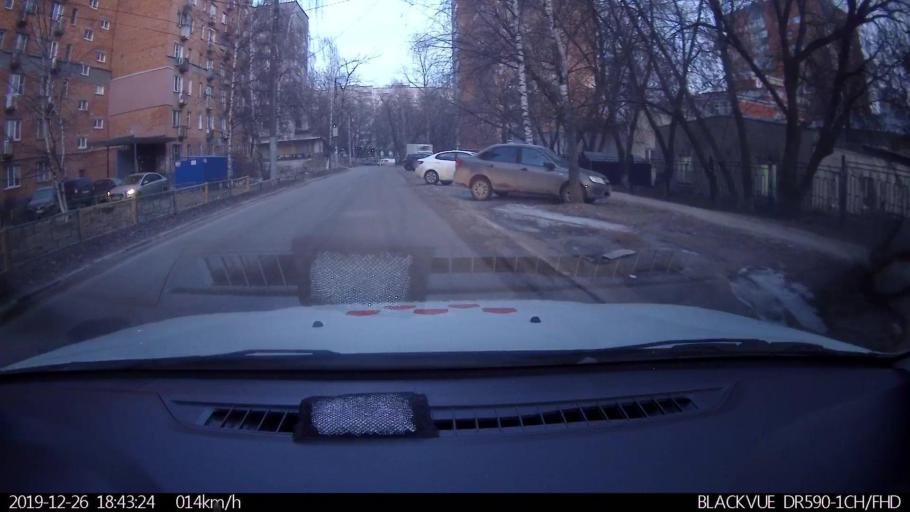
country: RU
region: Nizjnij Novgorod
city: Nizhniy Novgorod
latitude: 56.3184
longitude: 44.0296
